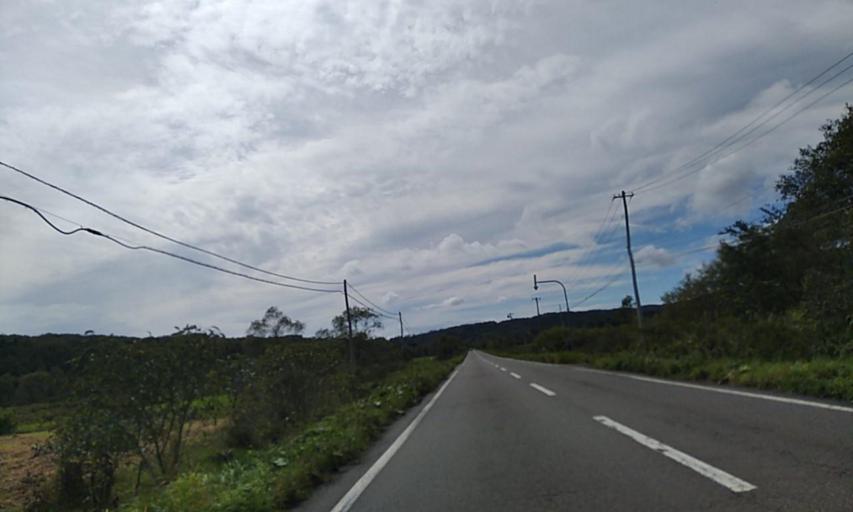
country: JP
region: Hokkaido
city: Kushiro
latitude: 42.8494
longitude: 143.8517
